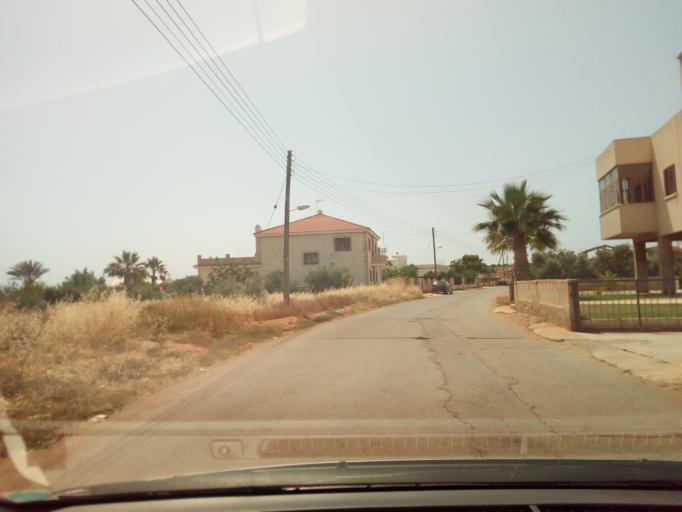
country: CY
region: Ammochostos
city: Liopetri
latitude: 34.9711
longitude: 33.8491
